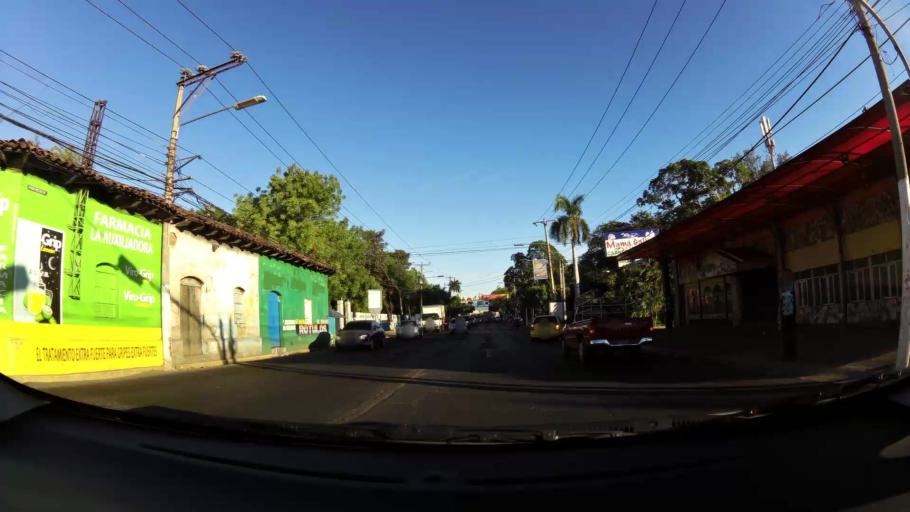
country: SV
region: San Miguel
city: San Miguel
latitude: 13.4809
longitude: -88.1849
